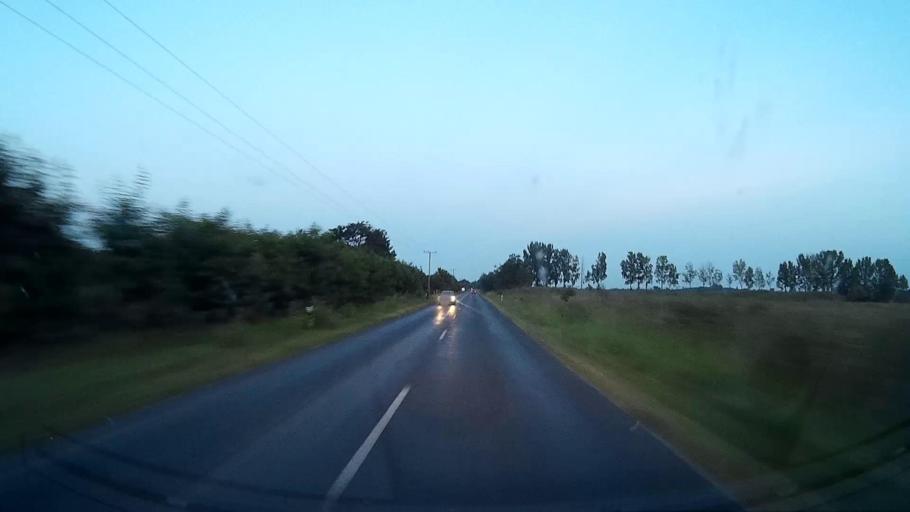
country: HU
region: Pest
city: Cegled
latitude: 47.1917
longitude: 19.7335
